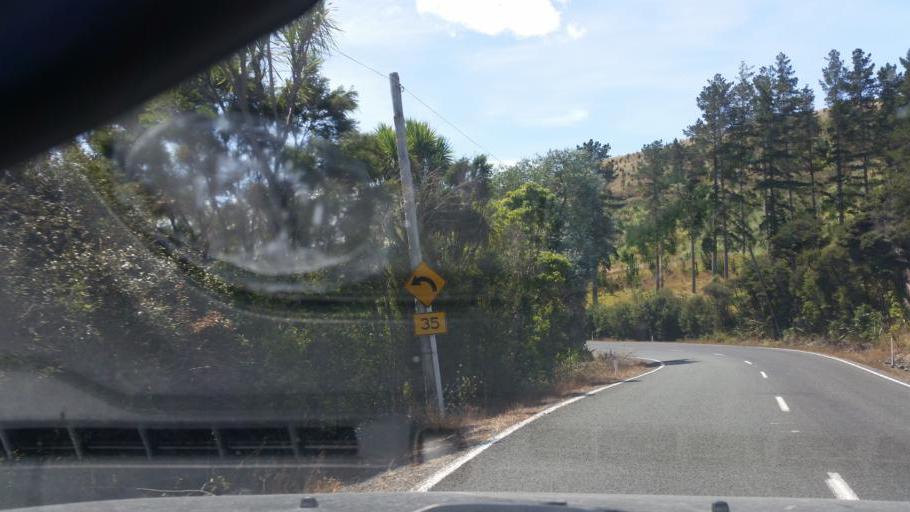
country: NZ
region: Auckland
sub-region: Auckland
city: Wellsford
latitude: -36.1771
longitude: 174.1670
